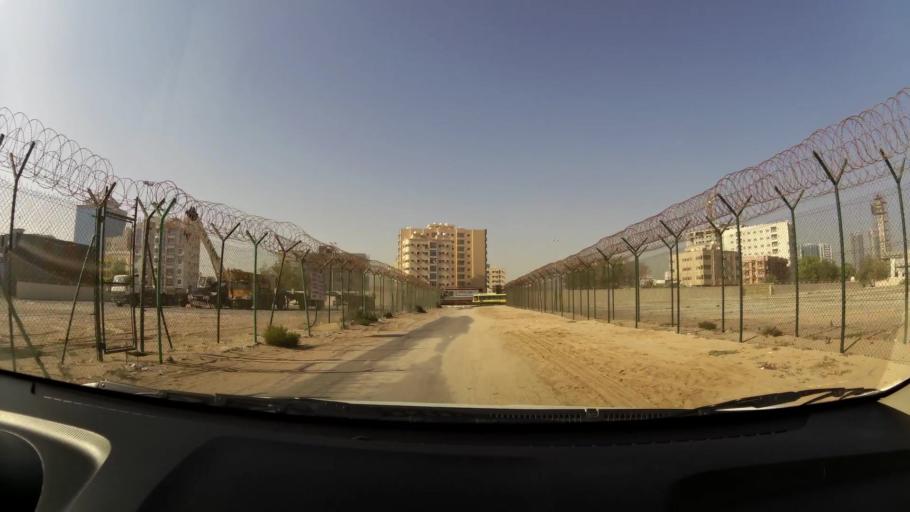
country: AE
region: Ajman
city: Ajman
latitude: 25.4214
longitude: 55.4506
